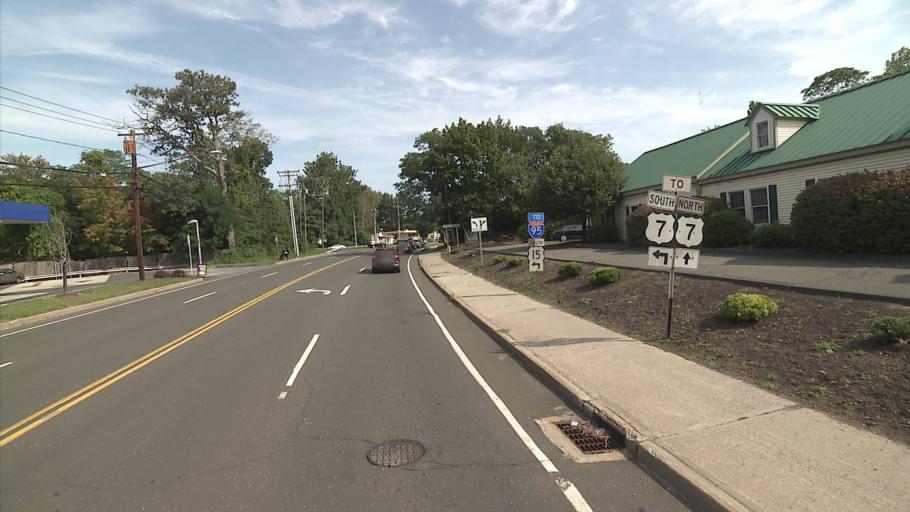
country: US
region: Connecticut
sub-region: Fairfield County
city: Norwalk
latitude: 41.1544
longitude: -73.4241
